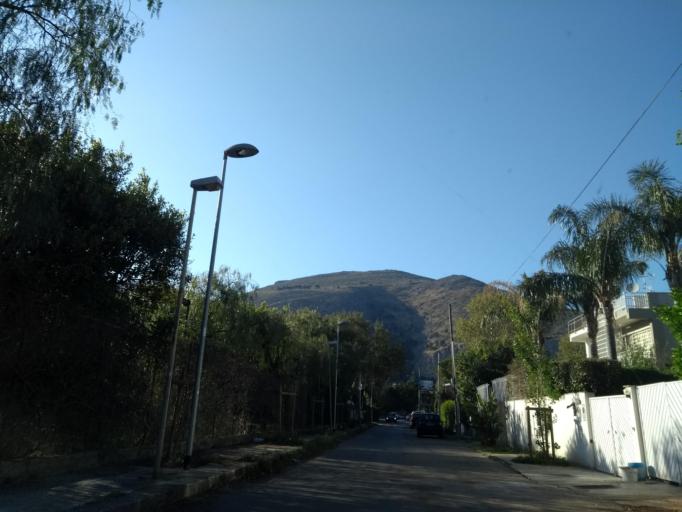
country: IT
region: Sicily
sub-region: Palermo
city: Palermo
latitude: 38.2005
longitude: 13.3243
